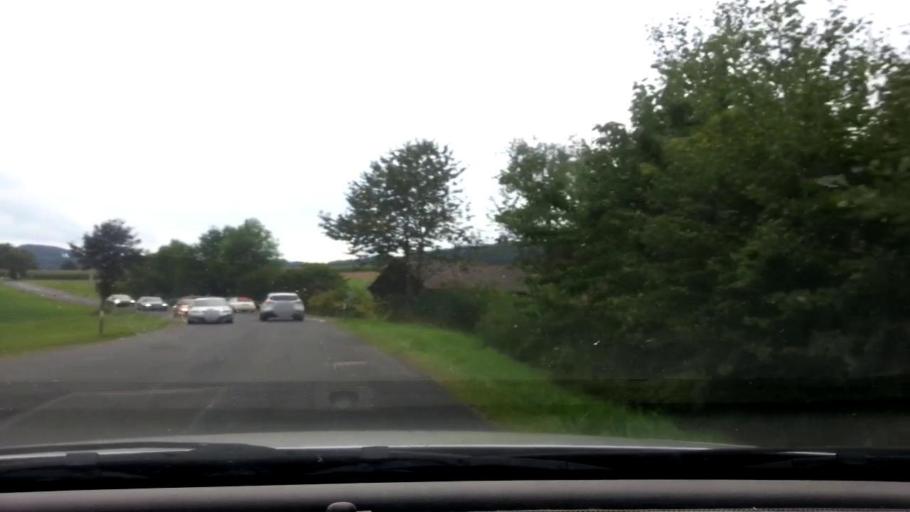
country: DE
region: Bavaria
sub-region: Upper Palatinate
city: Kemnath
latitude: 49.8686
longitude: 11.9342
